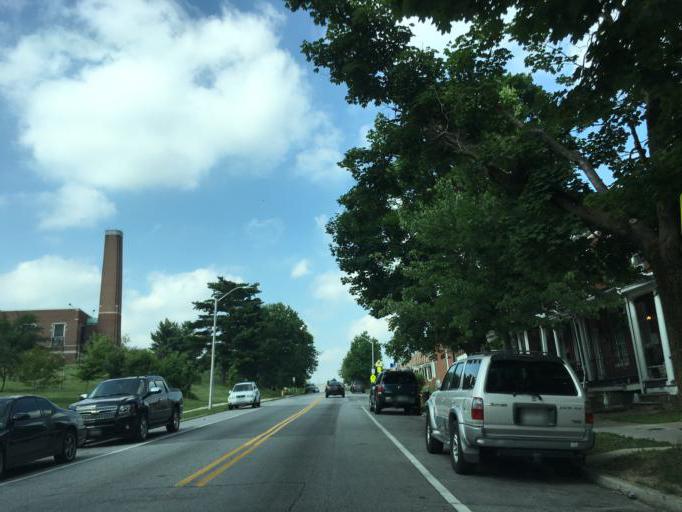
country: US
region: Maryland
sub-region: City of Baltimore
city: Baltimore
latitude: 39.3243
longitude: -76.5959
